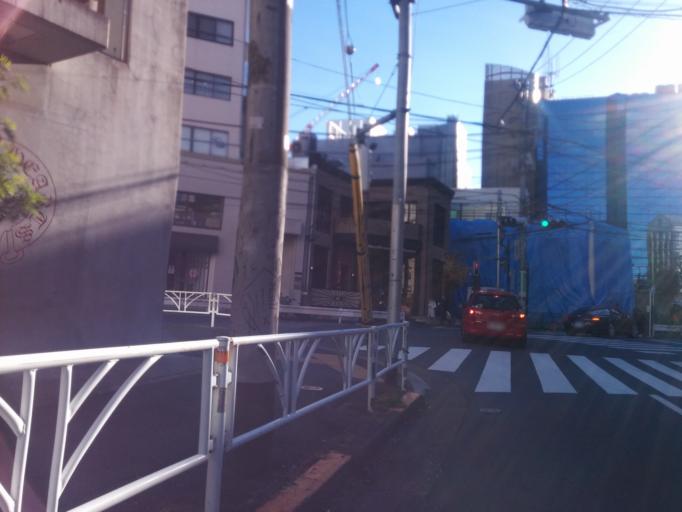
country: JP
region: Tokyo
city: Tokyo
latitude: 35.6723
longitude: 139.7091
